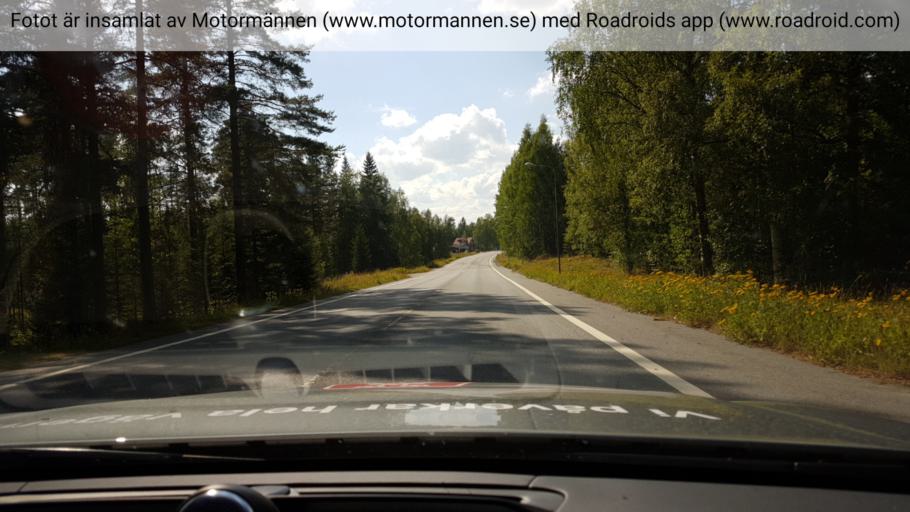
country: SE
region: Vaesterbotten
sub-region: Dorotea Kommun
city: Dorotea
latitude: 64.1065
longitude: 16.1925
